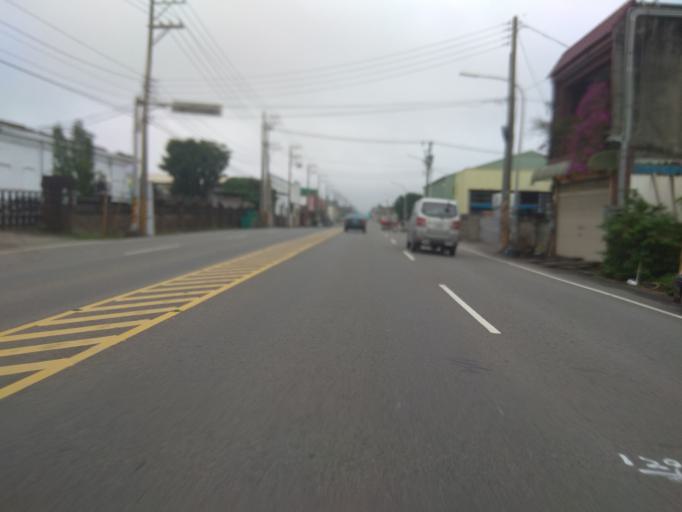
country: TW
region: Taiwan
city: Taoyuan City
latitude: 25.0225
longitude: 121.1173
